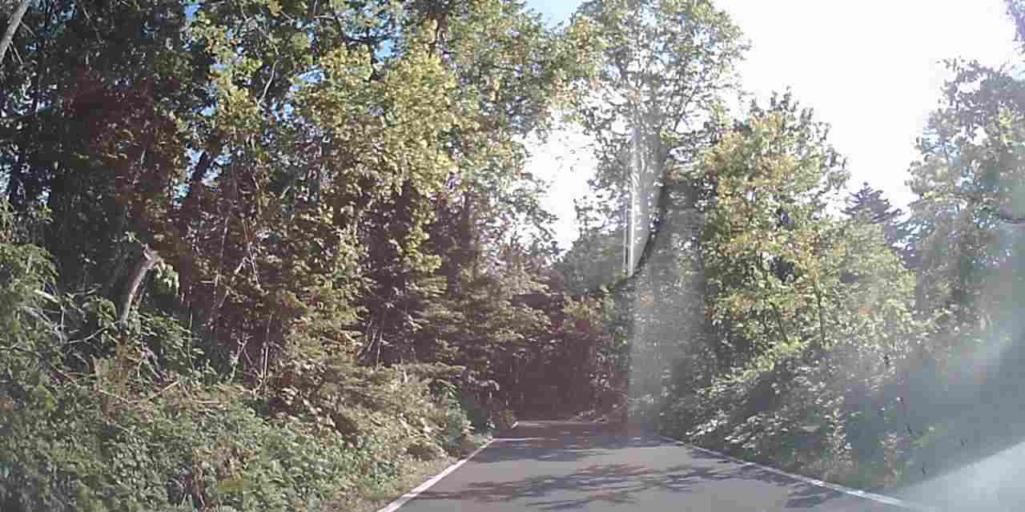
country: JP
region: Hokkaido
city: Shiraoi
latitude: 42.7379
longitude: 141.4109
